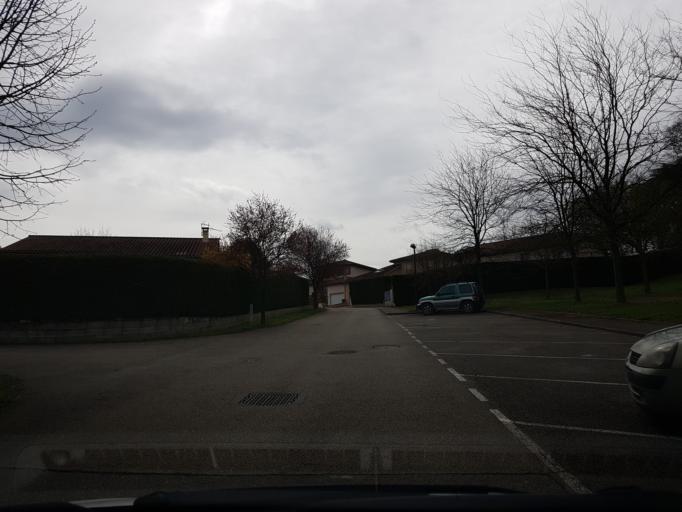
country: FR
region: Rhone-Alpes
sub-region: Departement de l'Ain
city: Trevoux
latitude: 45.9482
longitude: 4.7629
